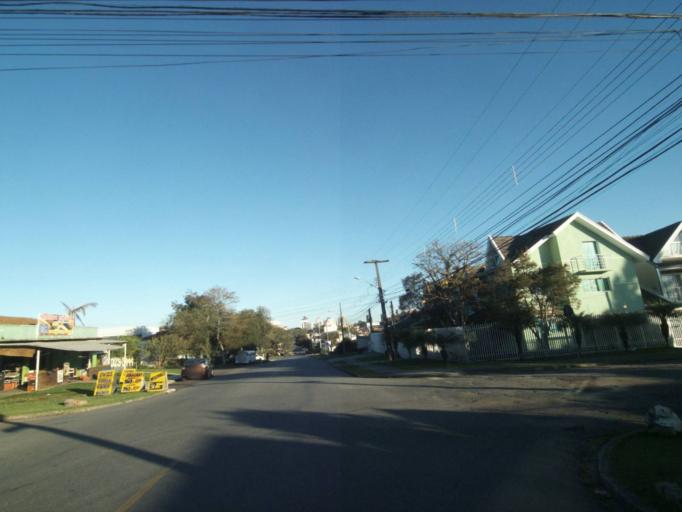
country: BR
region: Parana
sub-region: Curitiba
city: Curitiba
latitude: -25.3919
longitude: -49.2531
